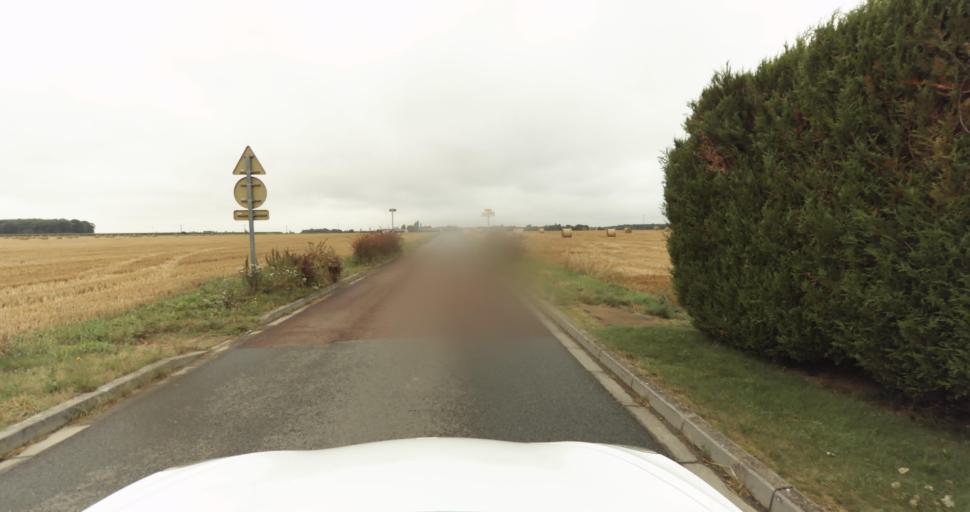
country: FR
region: Haute-Normandie
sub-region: Departement de l'Eure
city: Aviron
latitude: 49.0622
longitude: 1.1244
